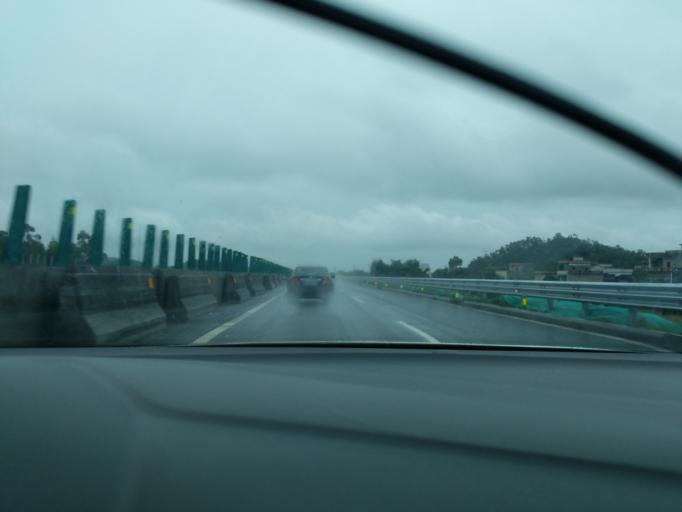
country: CN
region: Guangdong
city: Yueshan
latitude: 22.4624
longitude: 112.7234
